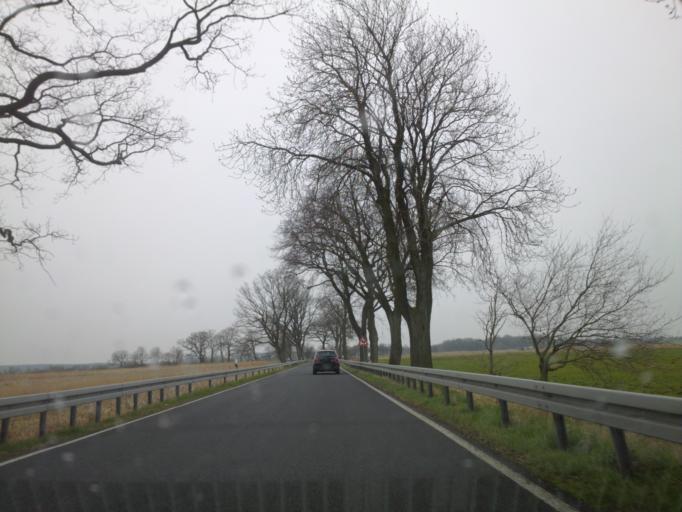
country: DE
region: Mecklenburg-Vorpommern
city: Bad Sulze
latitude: 54.1207
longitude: 12.6832
